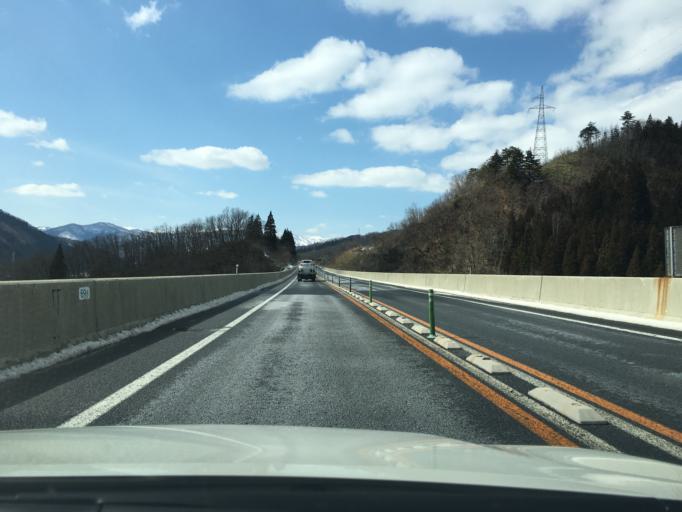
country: JP
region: Yamagata
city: Sagae
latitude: 38.4356
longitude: 140.1389
